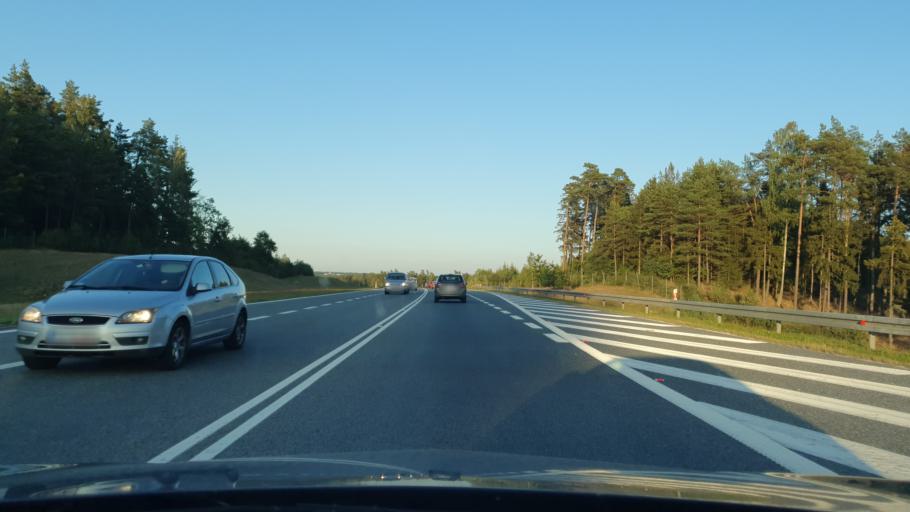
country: PL
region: Pomeranian Voivodeship
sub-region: Slupsk
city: Slupsk
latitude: 54.4308
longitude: 17.0532
